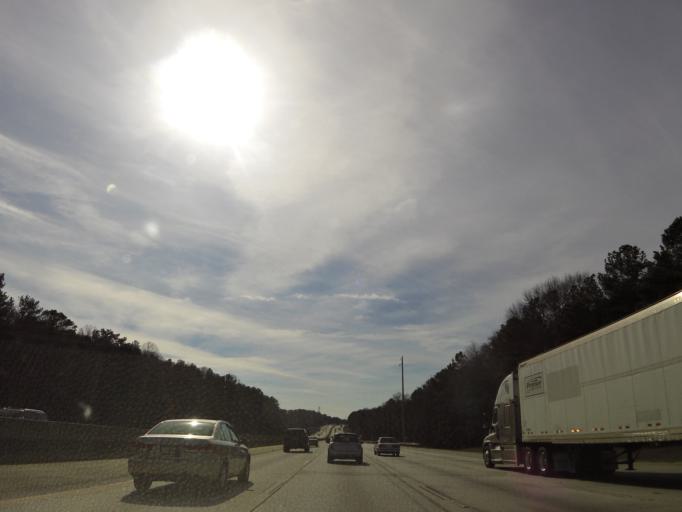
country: US
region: Georgia
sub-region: Fulton County
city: Union City
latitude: 33.6020
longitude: -84.4885
